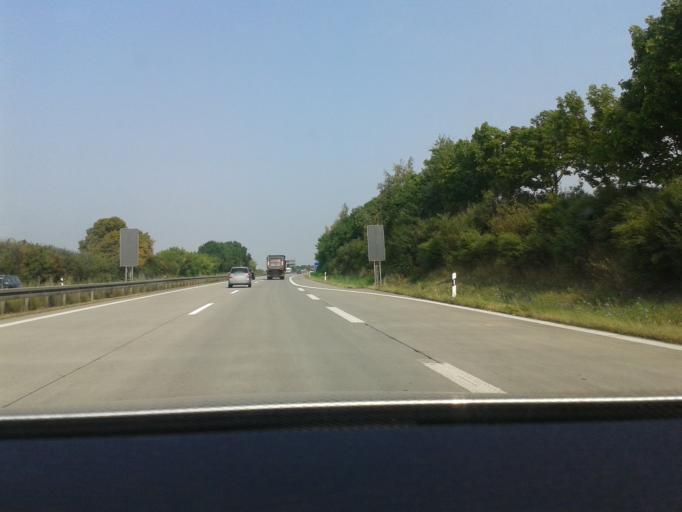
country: DE
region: Saxony
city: Nossen
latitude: 51.0597
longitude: 13.3379
